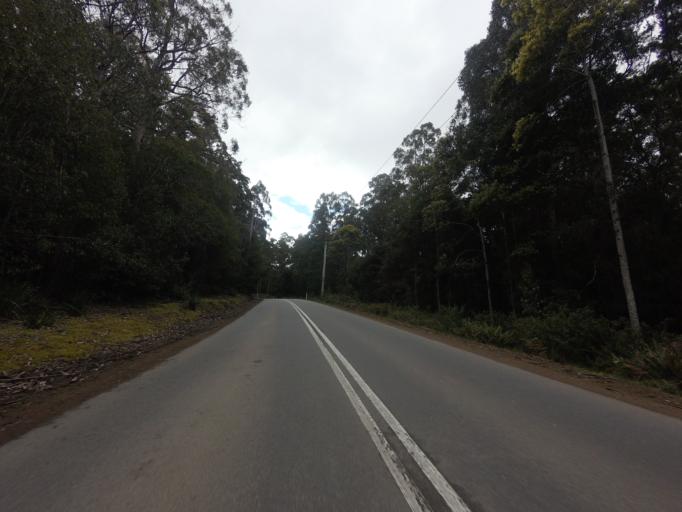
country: AU
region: Tasmania
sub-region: Huon Valley
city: Geeveston
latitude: -43.3825
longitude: 146.9614
